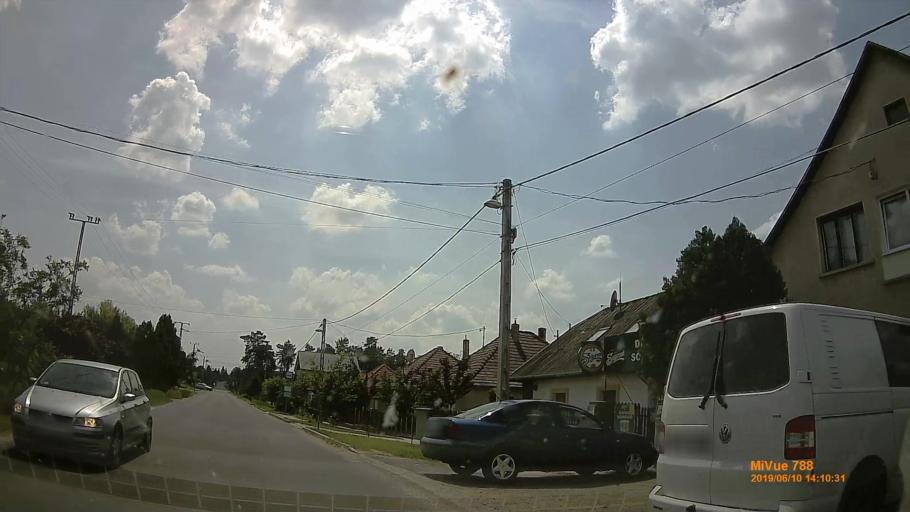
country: HU
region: Pest
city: God
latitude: 47.6785
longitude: 19.1444
